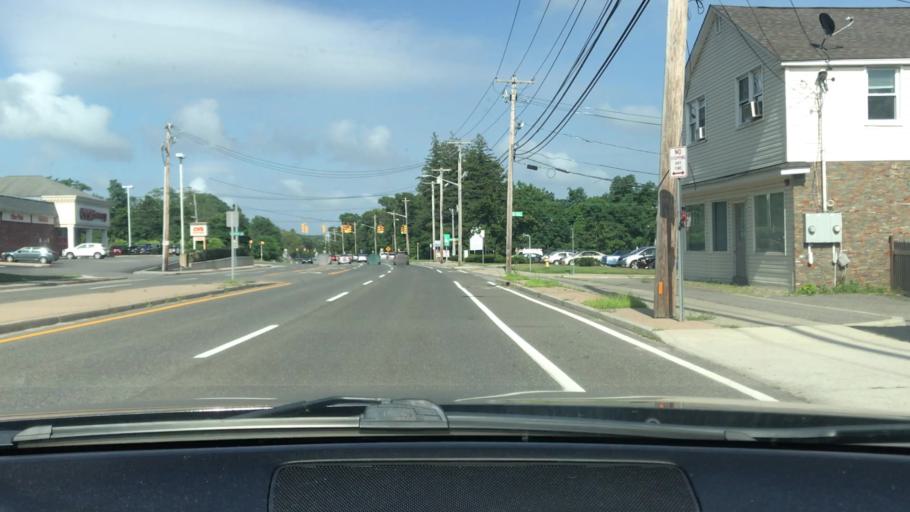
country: US
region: New York
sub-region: Suffolk County
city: Holbrook
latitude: 40.8320
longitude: -73.0833
